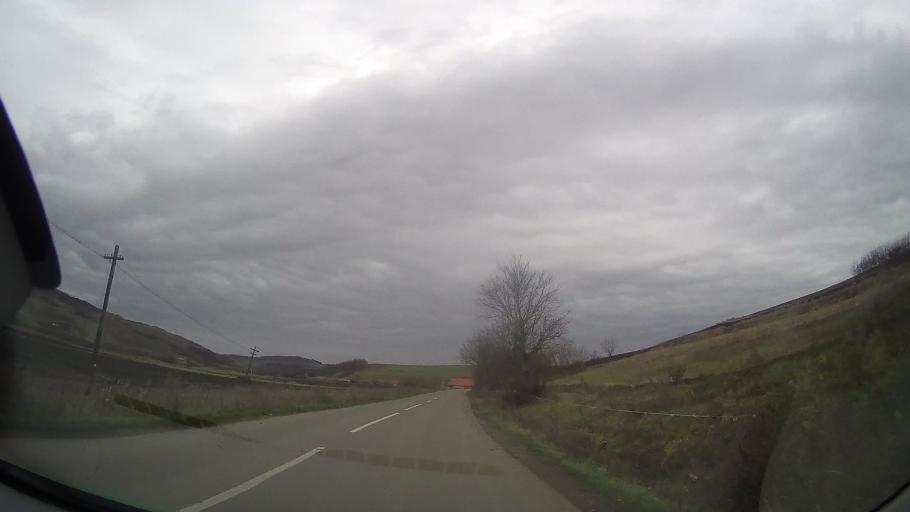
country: RO
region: Mures
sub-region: Comuna Craesti
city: Craiesti
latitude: 46.7754
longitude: 24.4259
